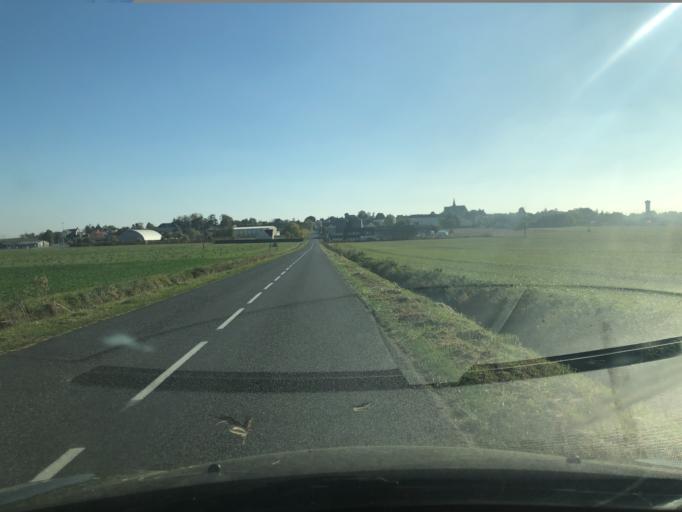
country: FR
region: Centre
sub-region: Departement d'Indre-et-Loire
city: Neuvy-le-Roi
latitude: 47.6111
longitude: 0.5967
